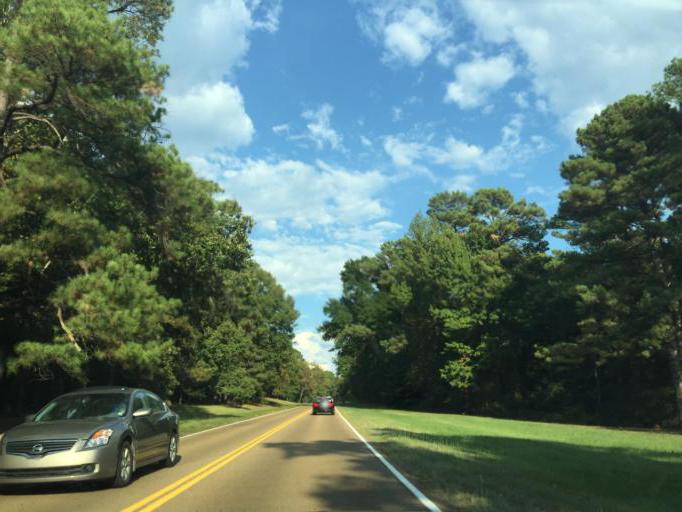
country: US
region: Mississippi
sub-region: Madison County
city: Ridgeland
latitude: 32.4268
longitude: -90.1236
